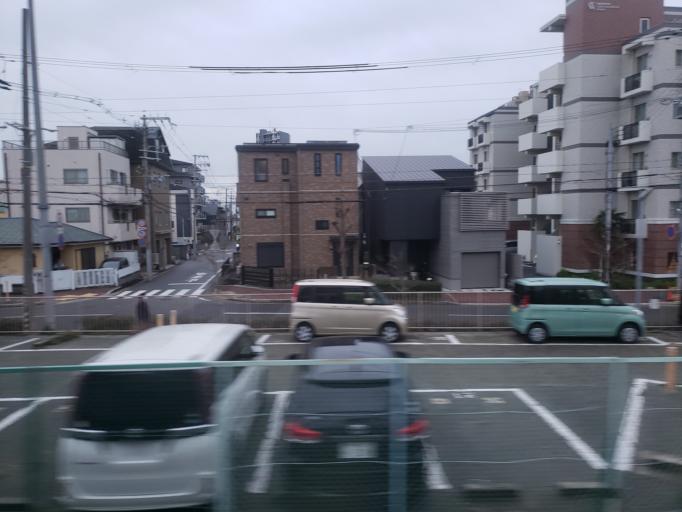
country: JP
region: Hyogo
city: Kobe
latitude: 34.6466
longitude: 135.1258
